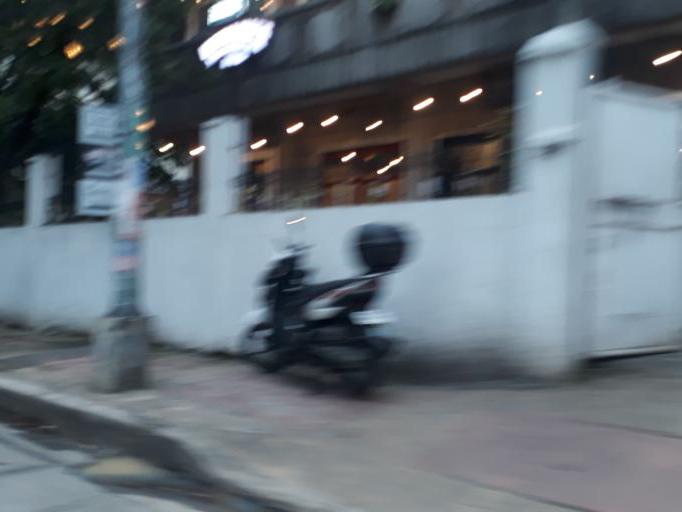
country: PH
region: Metro Manila
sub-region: Quezon City
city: Quezon City
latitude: 14.6799
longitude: 121.0812
